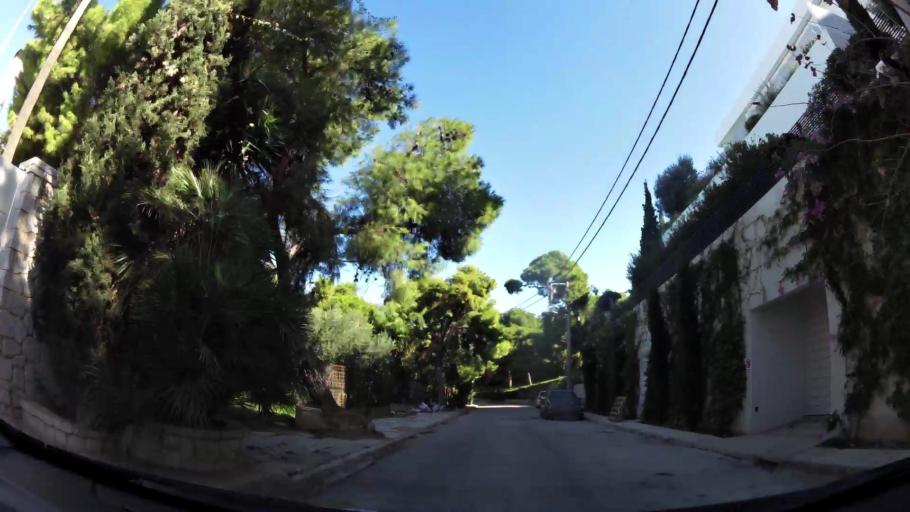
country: GR
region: Attica
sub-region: Nomarchia Anatolikis Attikis
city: Vouliagmeni
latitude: 37.8190
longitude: 23.7725
